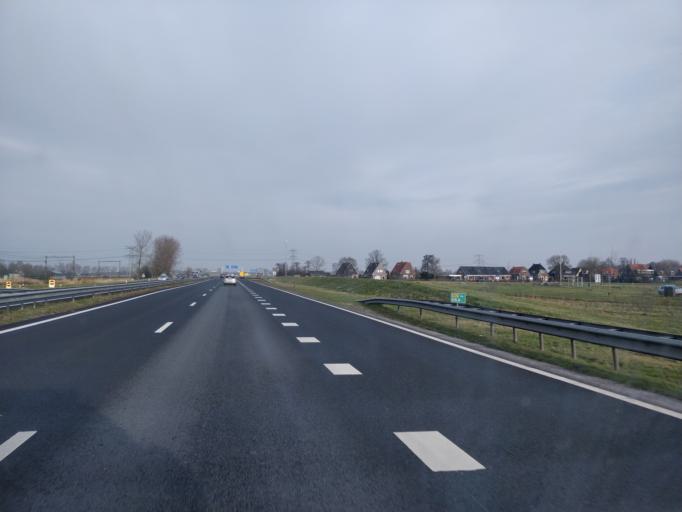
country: NL
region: Friesland
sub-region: Gemeente Leeuwarden
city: Wirdum
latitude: 53.1450
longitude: 5.7962
